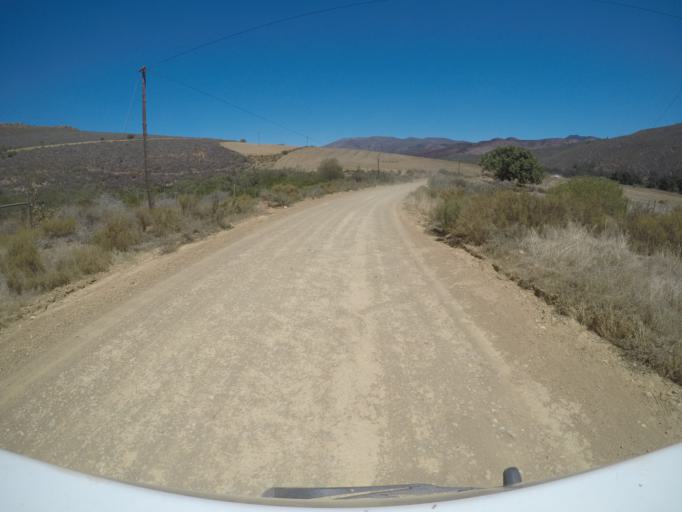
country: ZA
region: Western Cape
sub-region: Overberg District Municipality
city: Caledon
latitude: -34.1478
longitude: 19.2453
